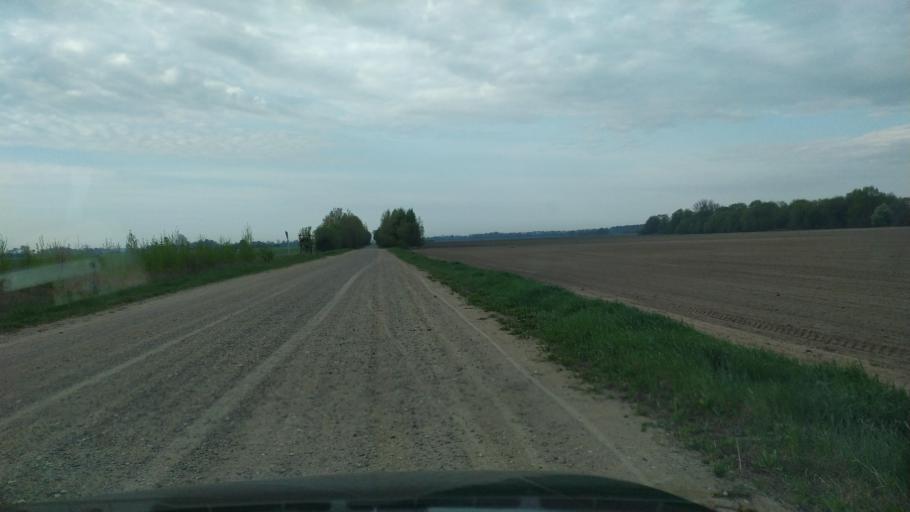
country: BY
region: Brest
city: Zhabinka
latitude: 52.1443
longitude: 24.0933
